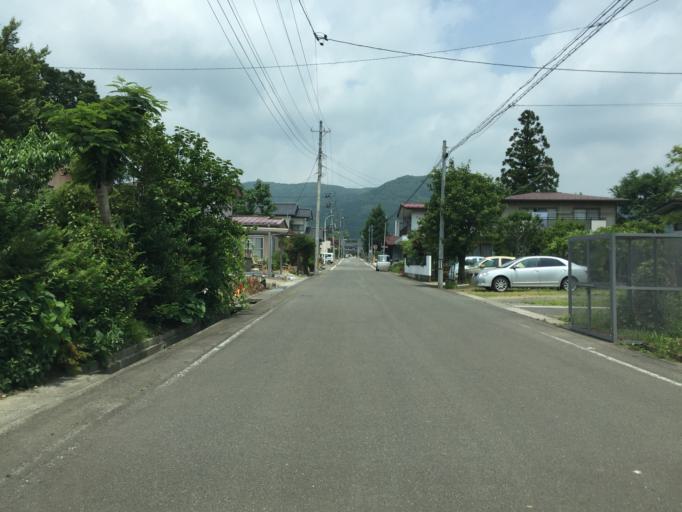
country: JP
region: Fukushima
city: Fukushima-shi
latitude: 37.7701
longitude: 140.3794
